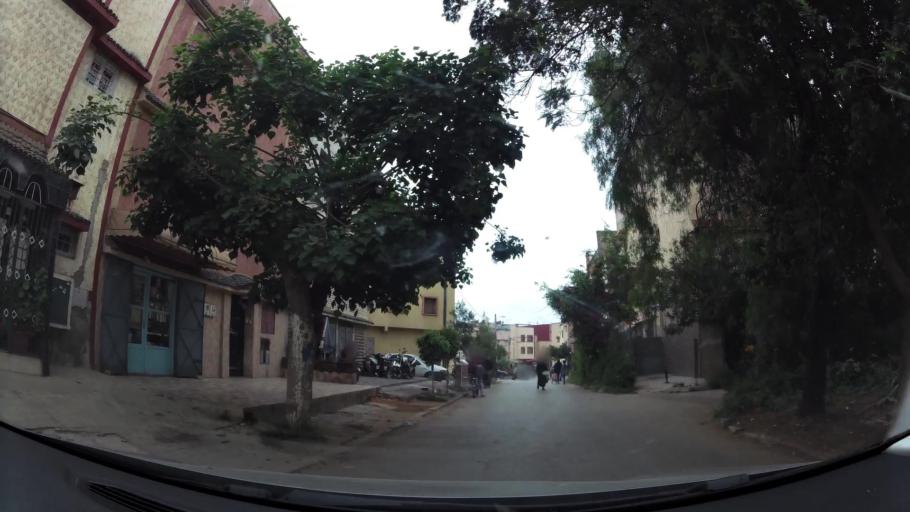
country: MA
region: Rabat-Sale-Zemmour-Zaer
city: Sale
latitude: 34.0472
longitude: -6.7952
